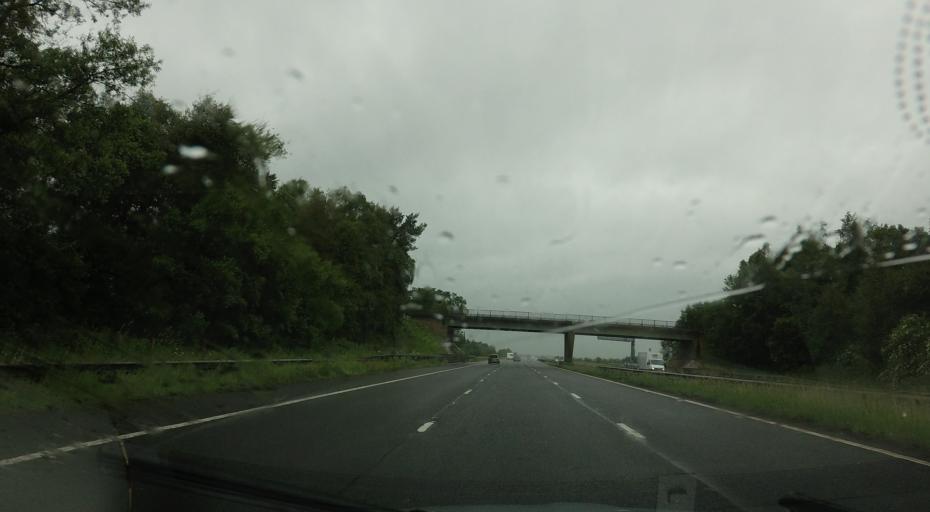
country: GB
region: Scotland
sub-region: Dumfries and Galloway
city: Gretna
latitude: 54.9676
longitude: -3.0005
